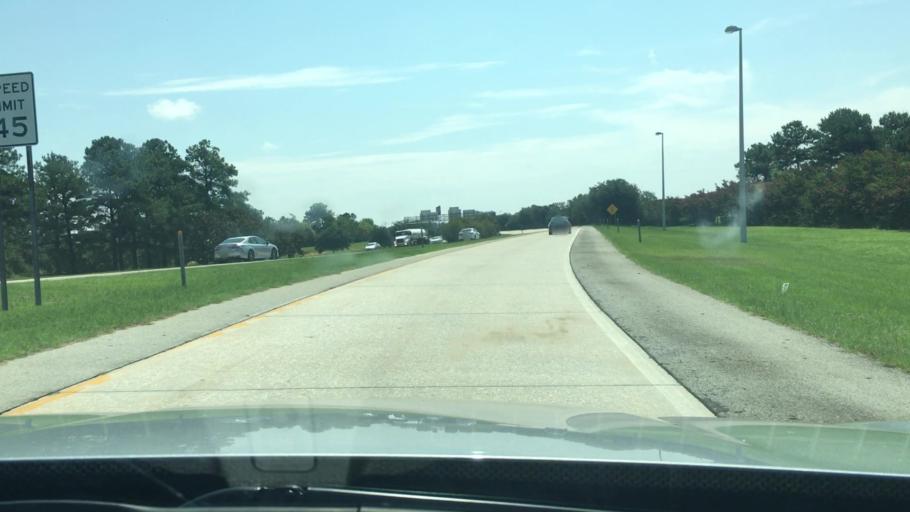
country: US
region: South Carolina
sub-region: Florence County
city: Florence
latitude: 34.1918
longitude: -79.8425
